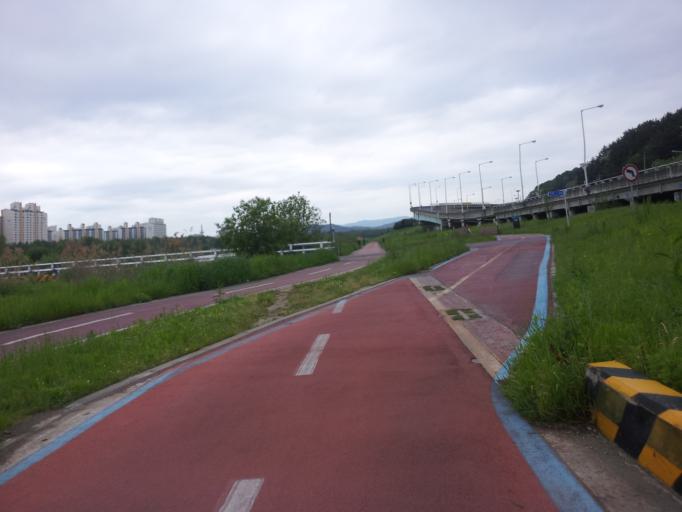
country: KR
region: Daejeon
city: Daejeon
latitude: 36.3605
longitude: 127.4021
